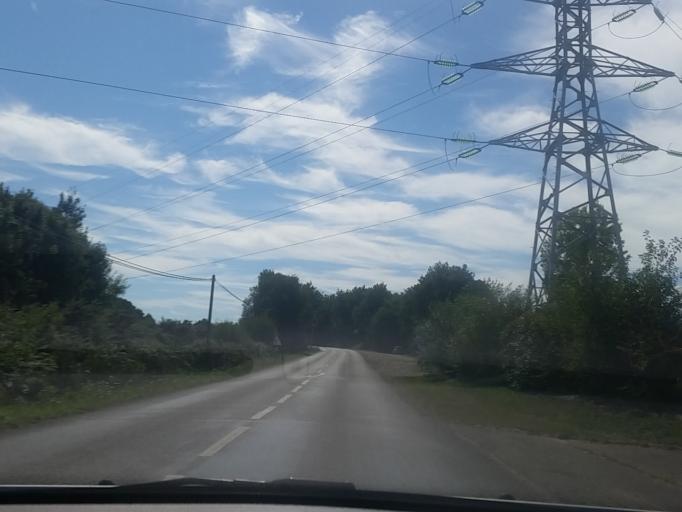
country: FR
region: Pays de la Loire
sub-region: Departement de la Loire-Atlantique
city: Saint-Pere-en-Retz
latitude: 47.2043
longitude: -2.0563
